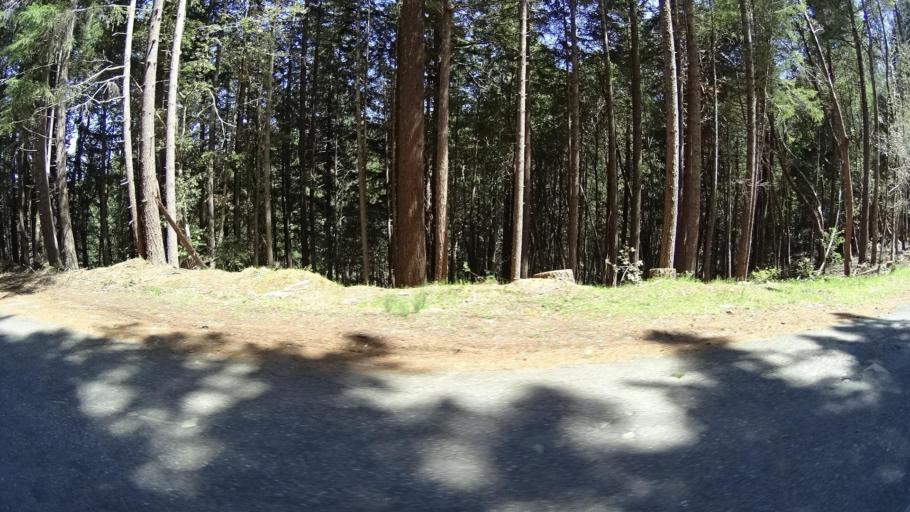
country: US
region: California
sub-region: Humboldt County
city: Rio Dell
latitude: 40.3064
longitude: -124.0622
